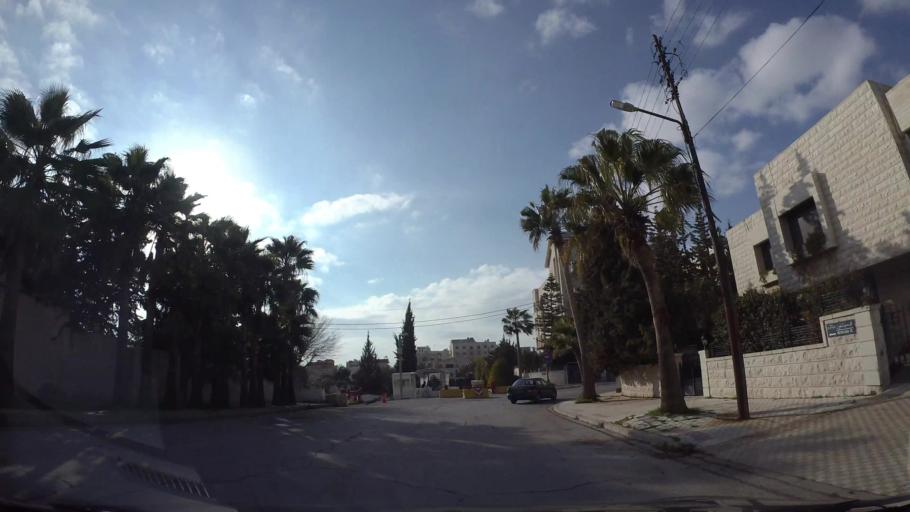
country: JO
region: Amman
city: Al Jubayhah
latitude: 31.9830
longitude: 35.8798
